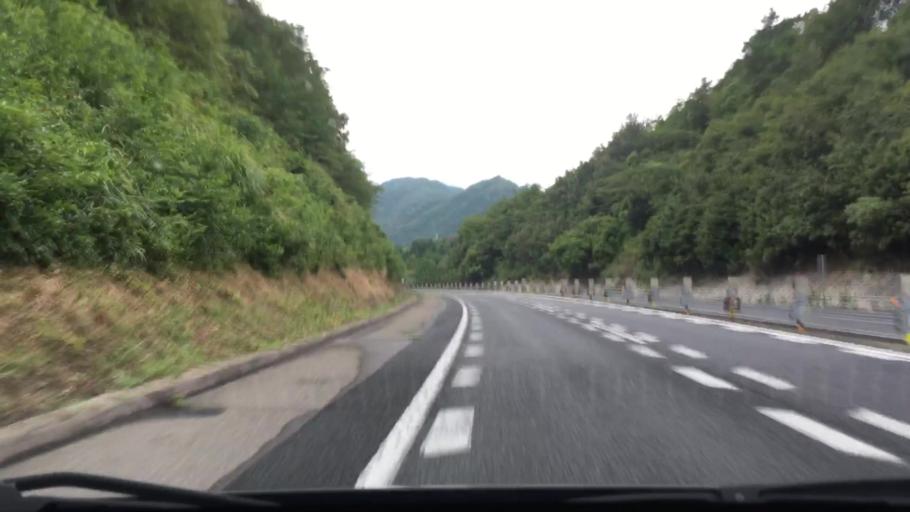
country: JP
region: Hiroshima
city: Hiroshima-shi
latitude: 34.6529
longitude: 132.5185
